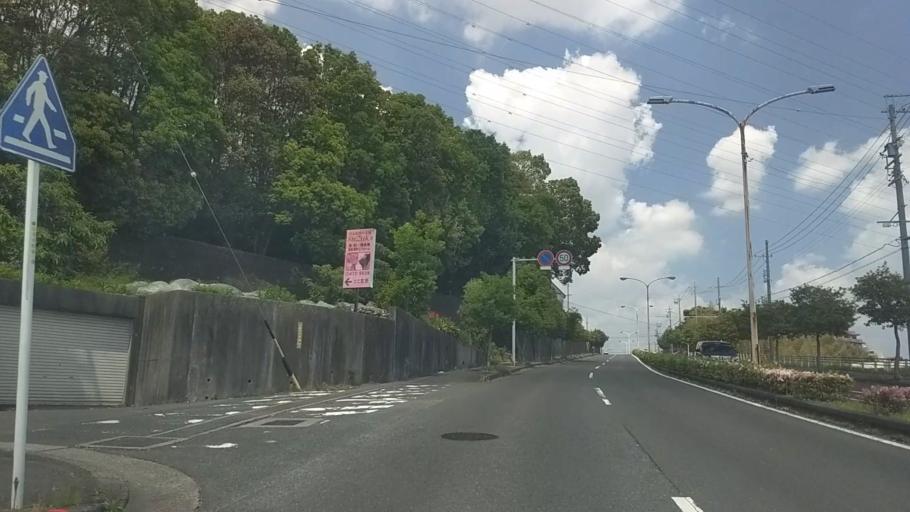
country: JP
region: Shizuoka
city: Hamamatsu
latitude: 34.7447
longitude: 137.7404
